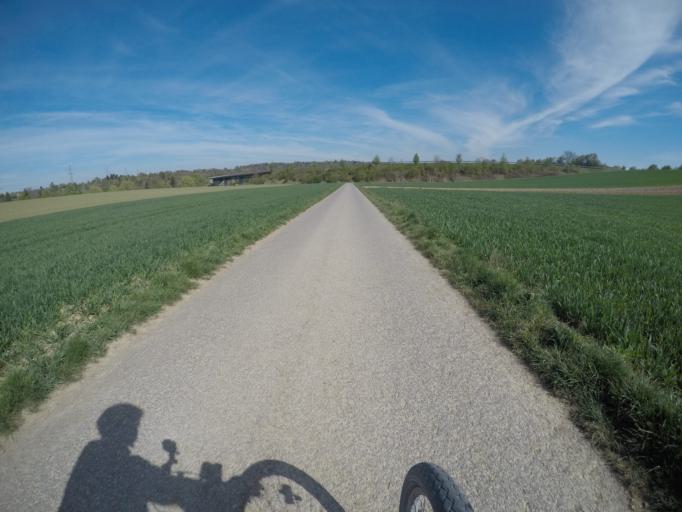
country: DE
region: Baden-Wuerttemberg
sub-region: Regierungsbezirk Stuttgart
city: Schwieberdingen
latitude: 48.8590
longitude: 9.0820
